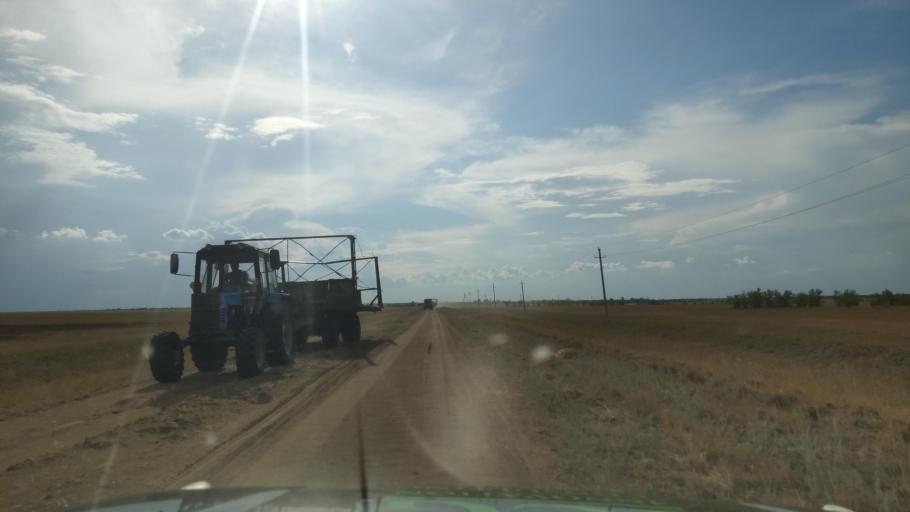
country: KZ
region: Pavlodar
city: Pavlodar
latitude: 52.5129
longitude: 77.4730
